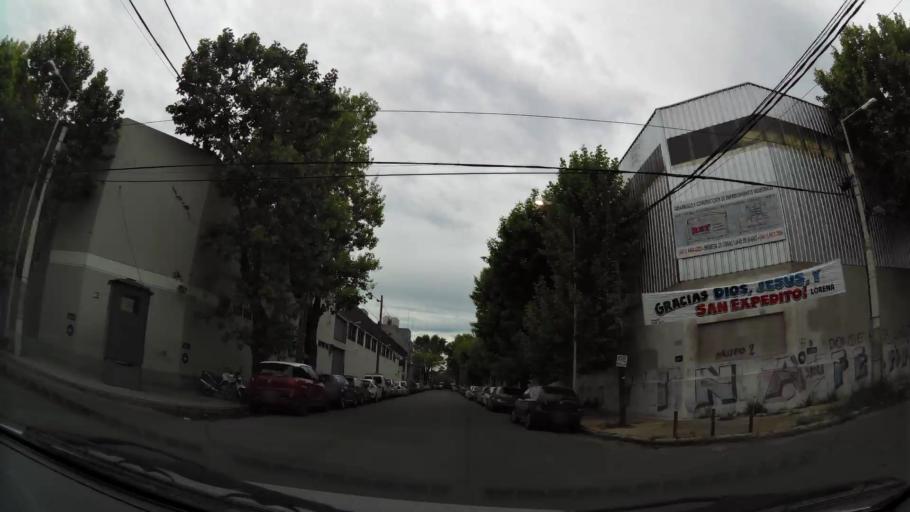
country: AR
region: Buenos Aires
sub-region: Partido de Avellaneda
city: Avellaneda
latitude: -34.6733
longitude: -58.3838
